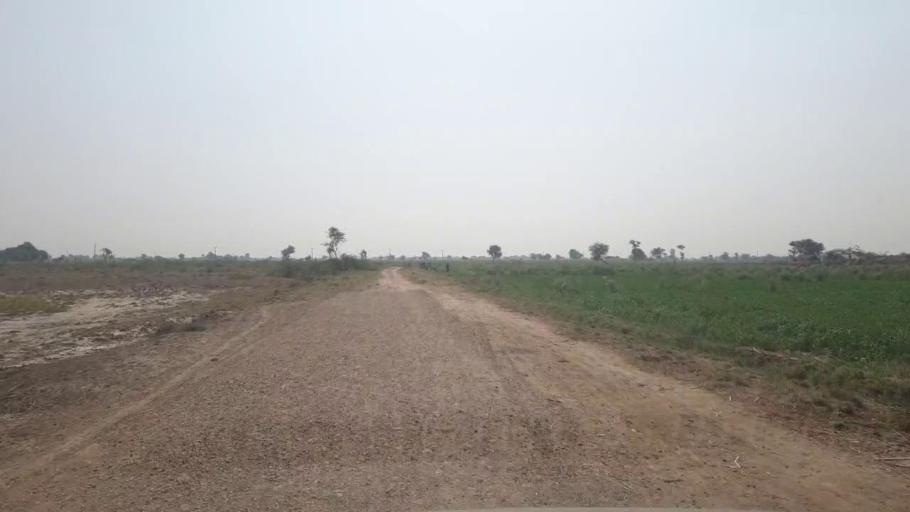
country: PK
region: Sindh
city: Dhoro Naro
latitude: 25.4492
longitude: 69.6219
